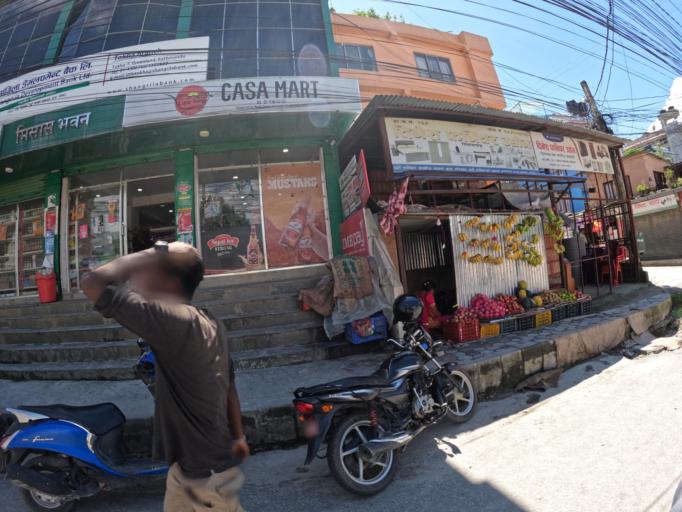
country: NP
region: Central Region
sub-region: Bagmati Zone
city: Kathmandu
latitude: 27.7464
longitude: 85.3257
